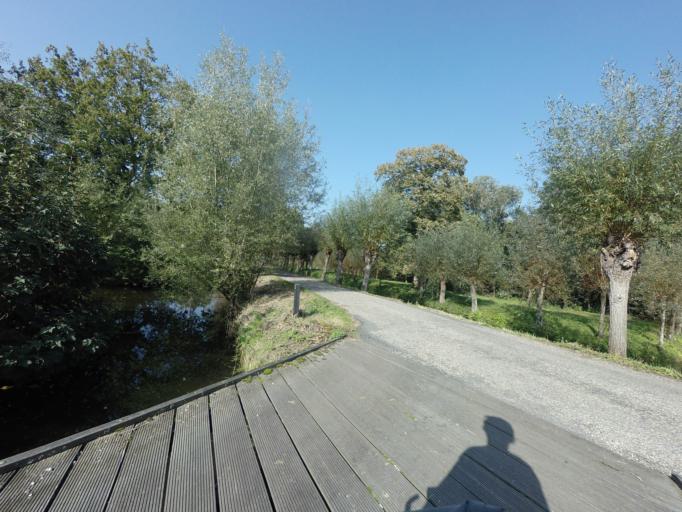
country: NL
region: Utrecht
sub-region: Gemeente Vianen
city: Vianen
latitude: 51.9598
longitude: 5.1118
